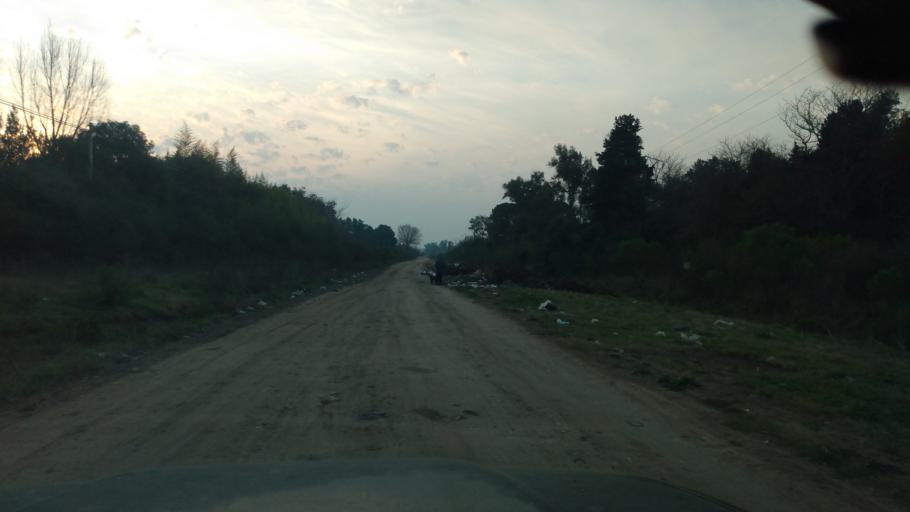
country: AR
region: Buenos Aires
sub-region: Partido de Lujan
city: Lujan
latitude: -34.5599
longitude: -59.1340
